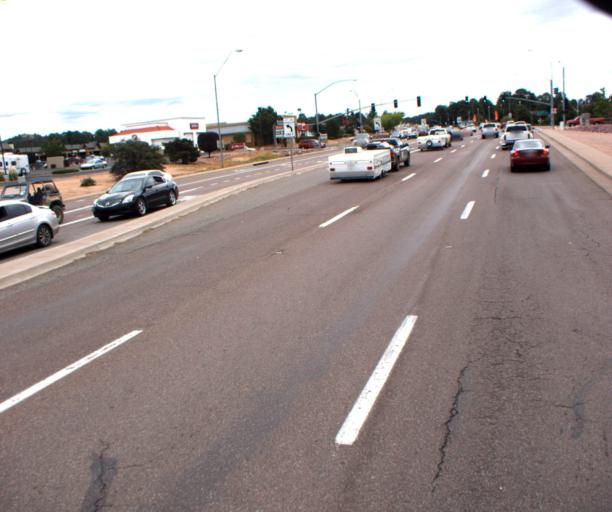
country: US
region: Arizona
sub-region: Gila County
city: Payson
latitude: 34.2405
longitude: -111.3216
